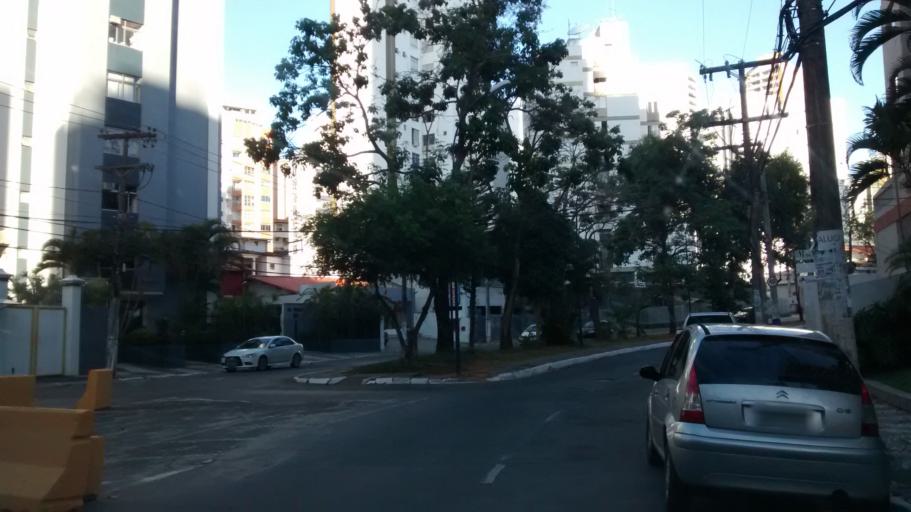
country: BR
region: Bahia
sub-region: Salvador
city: Salvador
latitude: -13.0040
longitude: -38.5189
